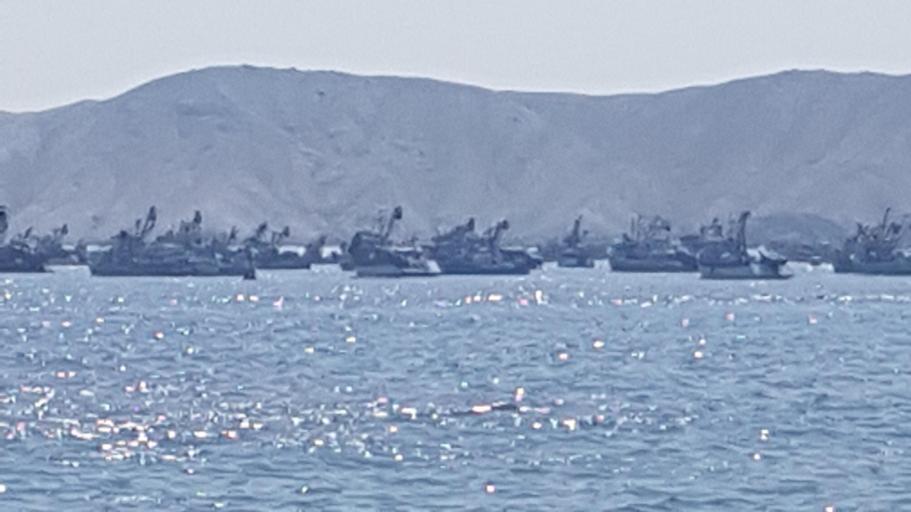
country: PE
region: Ancash
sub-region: Provincia de Santa
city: Chimbote
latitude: -9.0789
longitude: -78.5903
